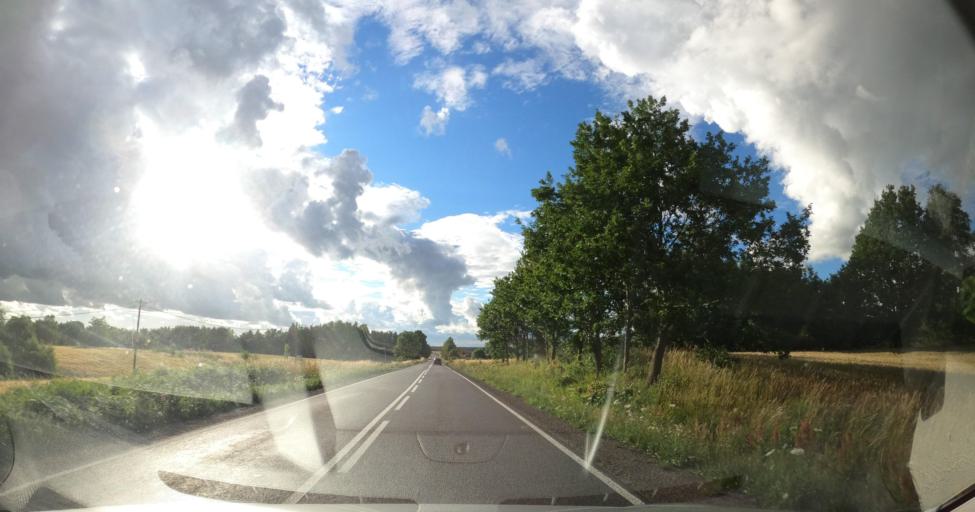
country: PL
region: Pomeranian Voivodeship
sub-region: Powiat bytowski
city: Czarna Dabrowka
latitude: 54.3491
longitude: 17.5815
